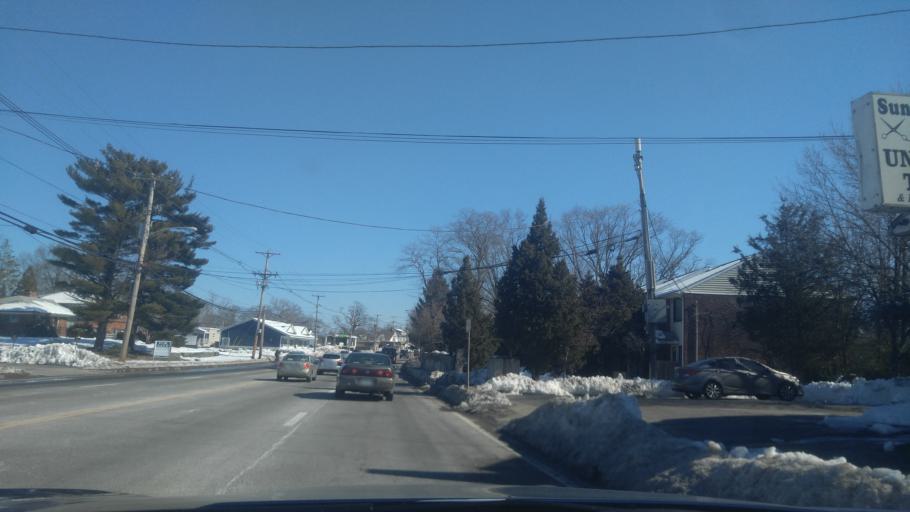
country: US
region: Rhode Island
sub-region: Providence County
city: Cranston
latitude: 41.7455
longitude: -71.4273
